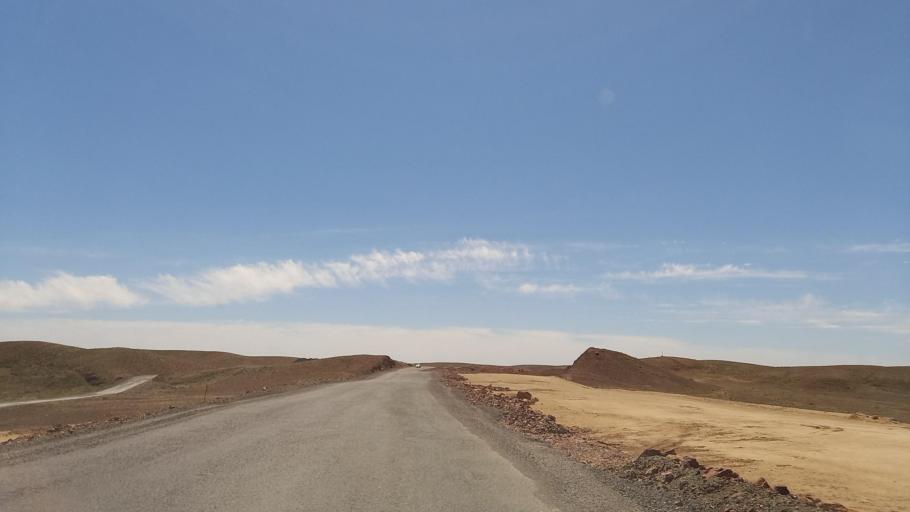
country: KZ
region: Almaty Oblysy
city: Ulken
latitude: 45.0646
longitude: 73.9995
